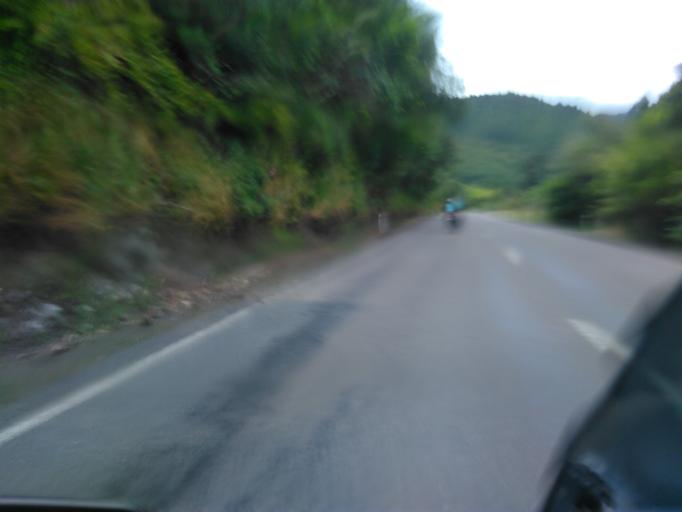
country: NZ
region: Bay of Plenty
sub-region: Opotiki District
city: Opotiki
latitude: -38.2903
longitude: 177.3713
